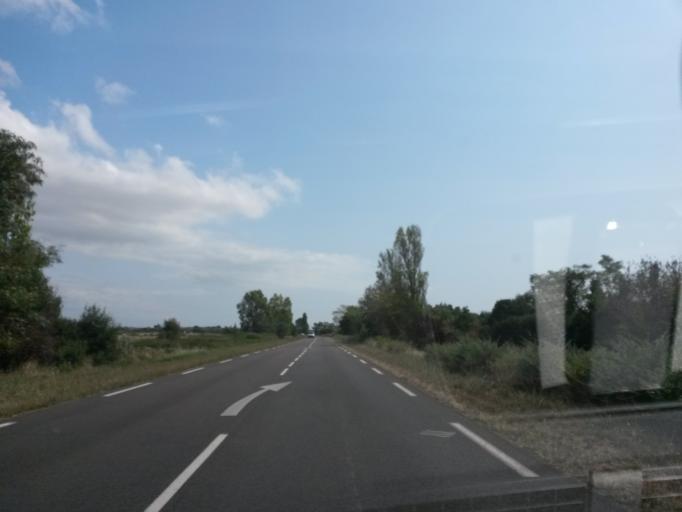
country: FR
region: Pays de la Loire
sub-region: Departement de la Vendee
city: La Tranche-sur-Mer
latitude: 46.3592
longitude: -1.4469
